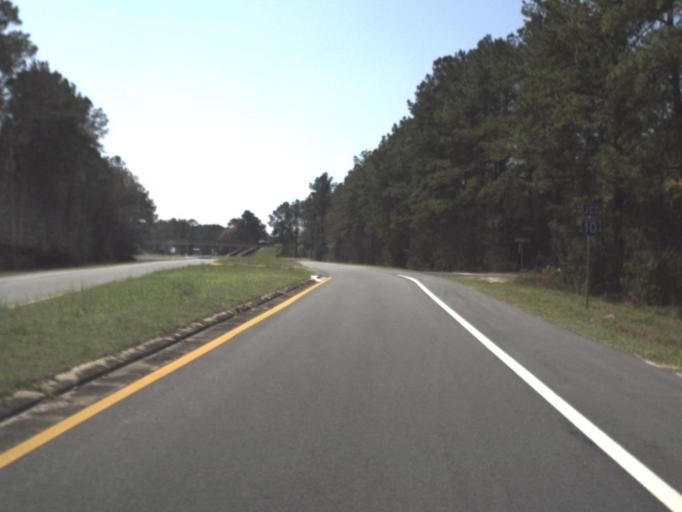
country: US
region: Florida
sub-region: Jefferson County
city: Monticello
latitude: 30.4917
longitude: -84.0262
